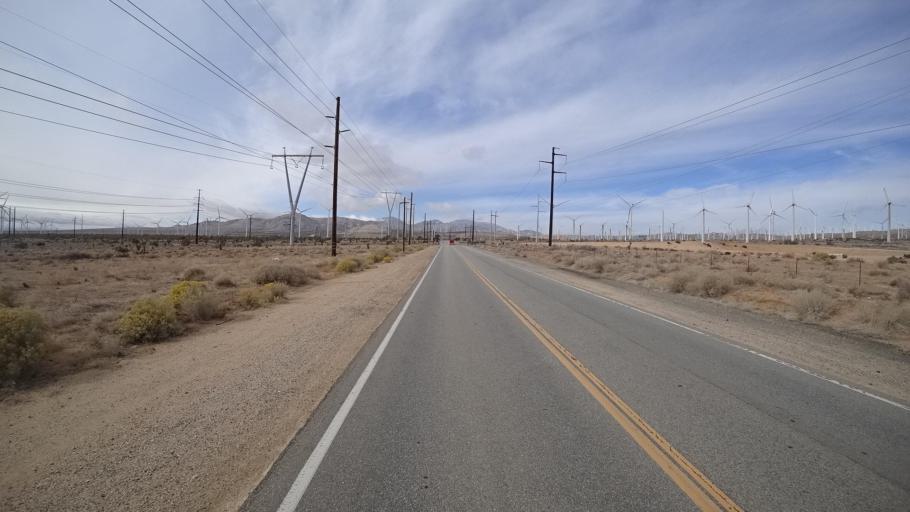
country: US
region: California
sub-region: Kern County
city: Mojave
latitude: 35.0384
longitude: -118.2883
